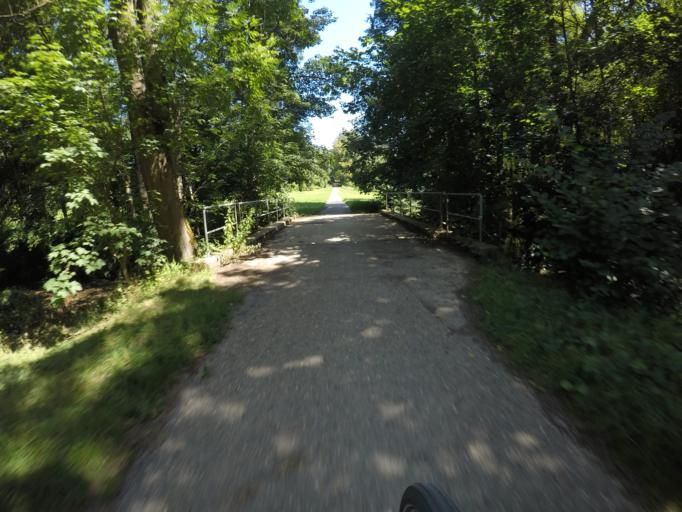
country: DE
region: Baden-Wuerttemberg
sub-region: Regierungsbezirk Stuttgart
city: Leinfelden-Echterdingen
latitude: 48.7097
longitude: 9.1832
